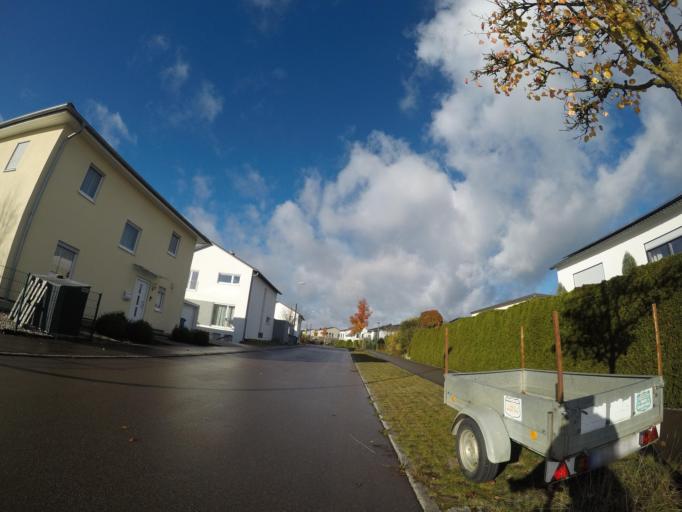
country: DE
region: Baden-Wuerttemberg
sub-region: Tuebingen Region
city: Ulm
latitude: 48.4409
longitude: 9.9958
